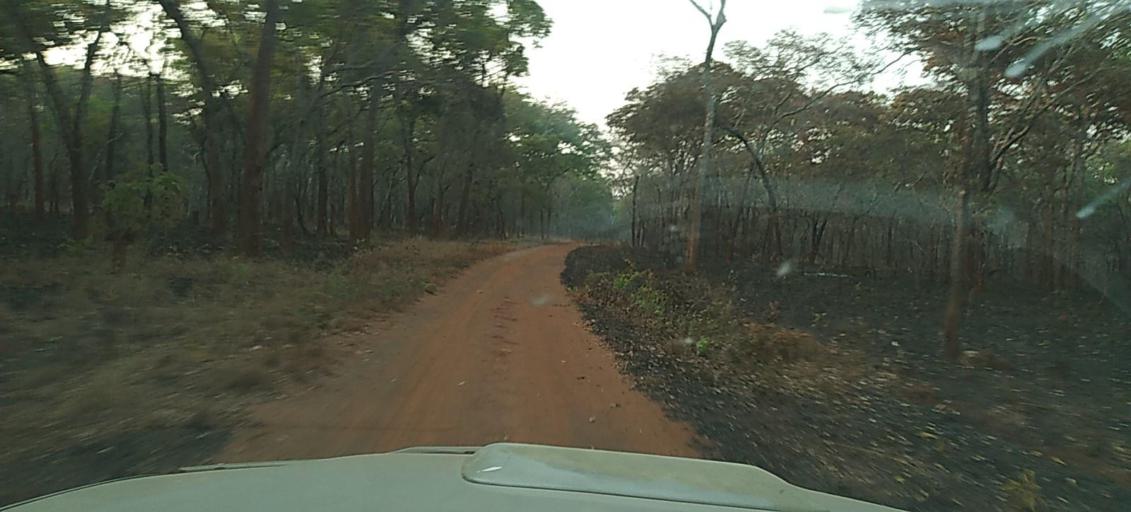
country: ZM
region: North-Western
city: Kasempa
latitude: -13.1091
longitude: 26.4051
